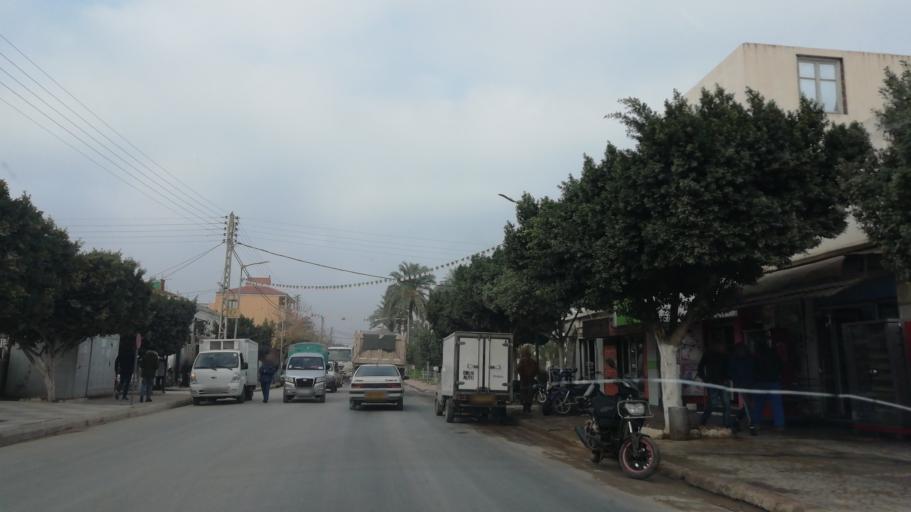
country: DZ
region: Relizane
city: Djidiouia
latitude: 35.9296
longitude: 0.8337
